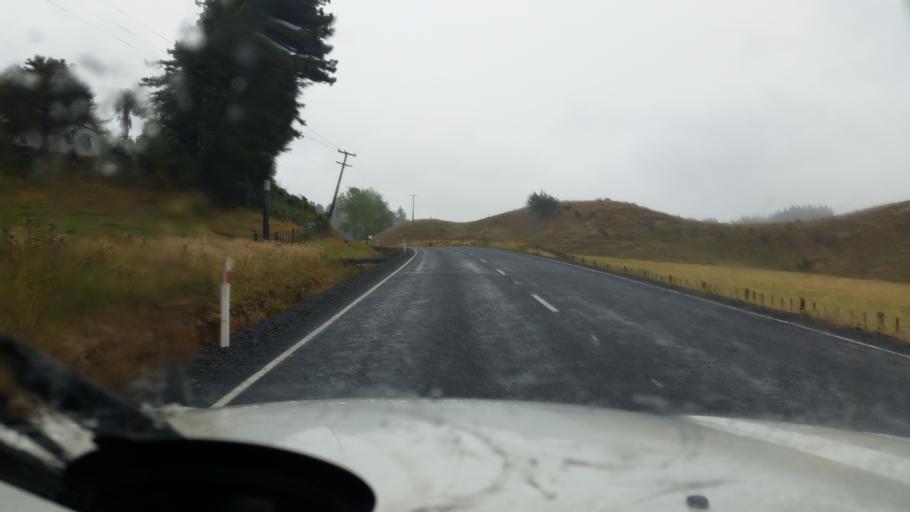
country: NZ
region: Northland
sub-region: Far North District
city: Kaitaia
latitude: -35.2744
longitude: 173.3512
